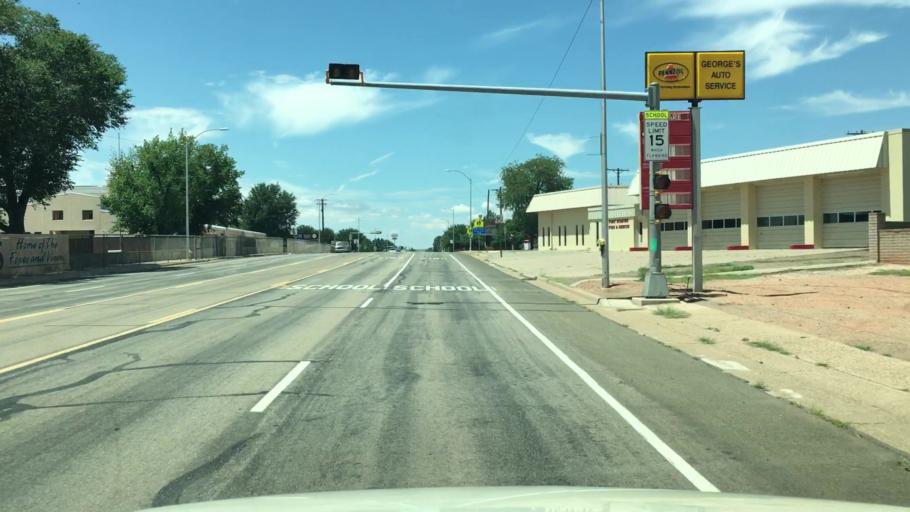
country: US
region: New Mexico
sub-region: De Baca County
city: Fort Sumner
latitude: 34.4691
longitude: -104.2370
